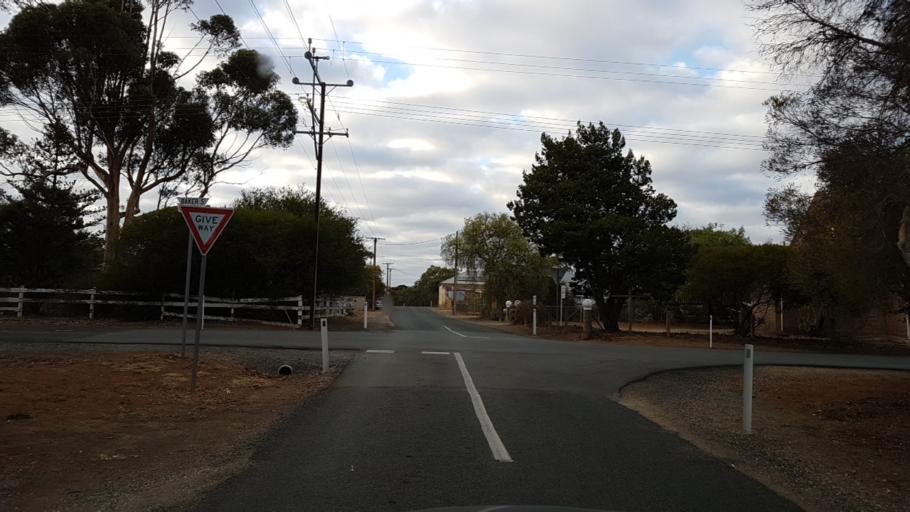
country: AU
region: South Australia
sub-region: Mount Barker
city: Callington
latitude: -35.1158
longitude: 139.0380
